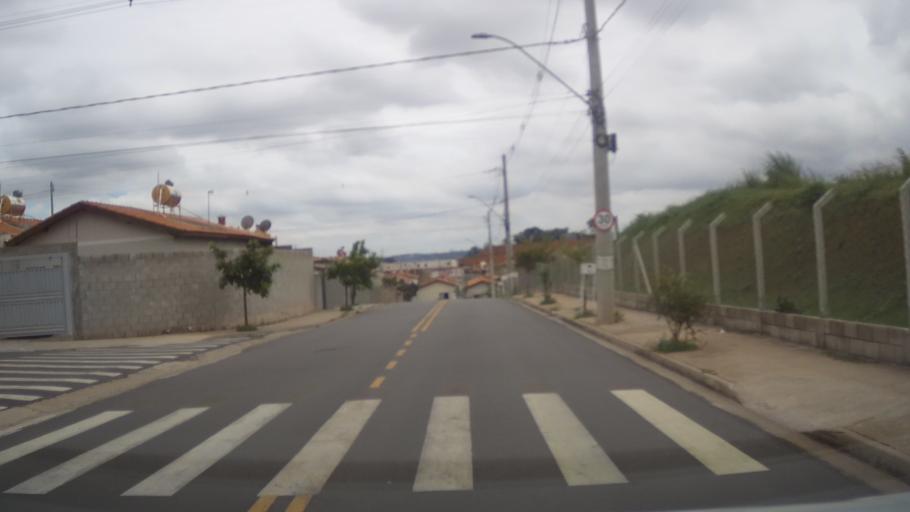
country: BR
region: Sao Paulo
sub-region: Louveira
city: Louveira
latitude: -23.0840
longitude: -46.9885
